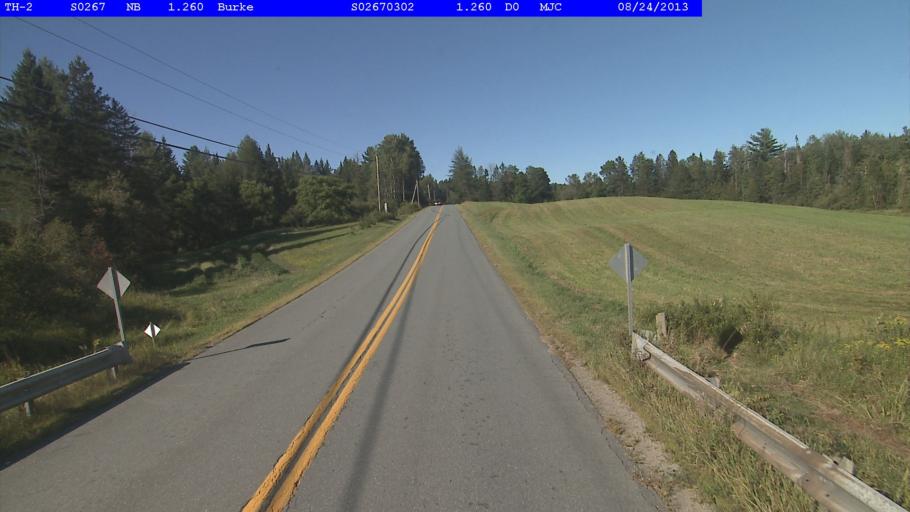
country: US
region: Vermont
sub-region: Caledonia County
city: Lyndonville
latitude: 44.6044
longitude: -71.9388
